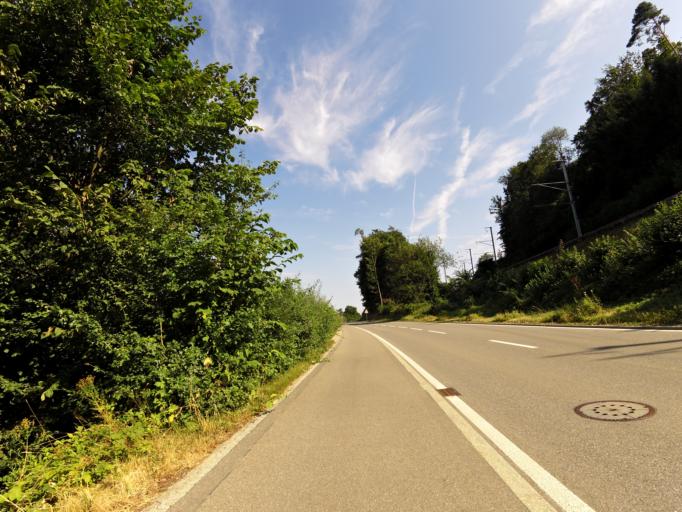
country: CH
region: Zug
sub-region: Zug
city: Walchwil
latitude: 47.1214
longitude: 8.4962
